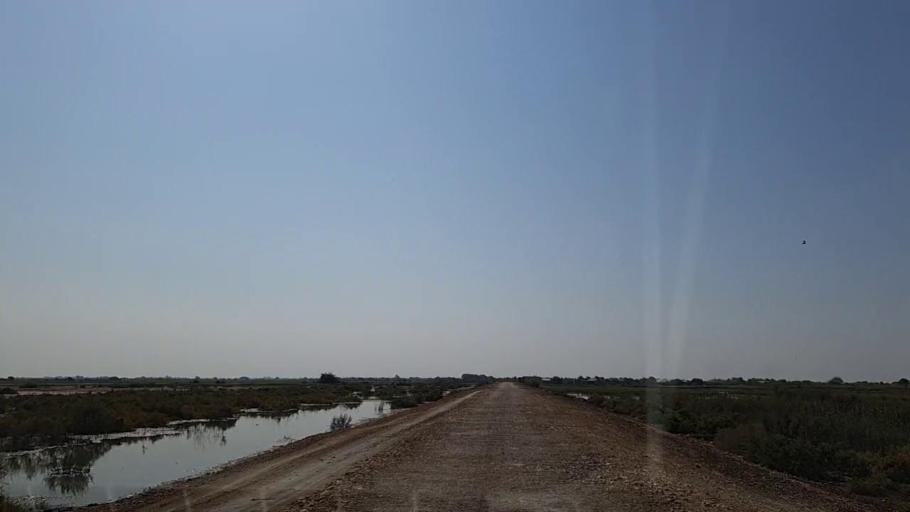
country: PK
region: Sindh
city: Chuhar Jamali
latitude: 24.4773
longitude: 68.0914
